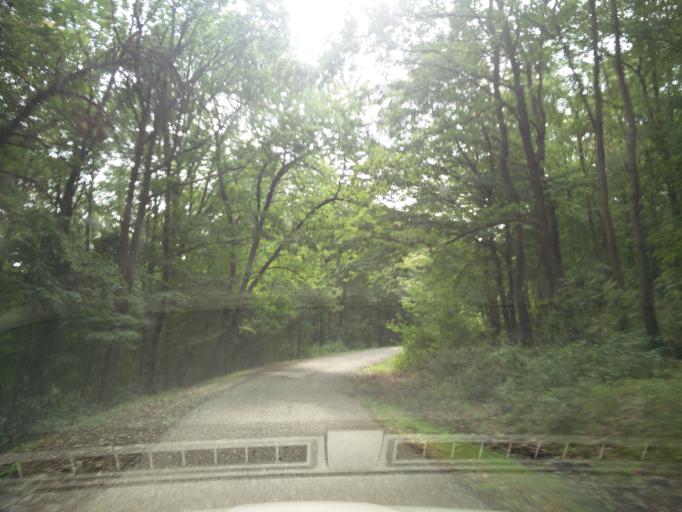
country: HU
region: Pest
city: Nagykovacsi
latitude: 47.6902
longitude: 18.9996
